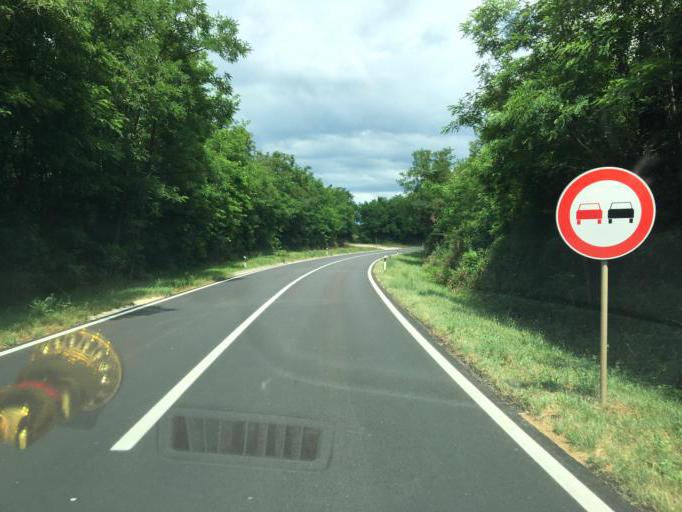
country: HR
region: Istarska
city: Karojba
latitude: 45.2437
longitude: 13.8574
